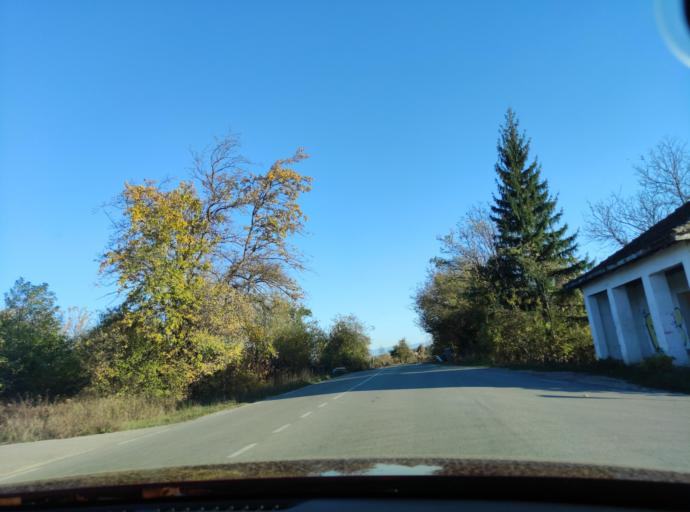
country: BG
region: Montana
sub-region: Obshtina Chiprovtsi
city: Chiprovtsi
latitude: 43.4226
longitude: 23.0160
